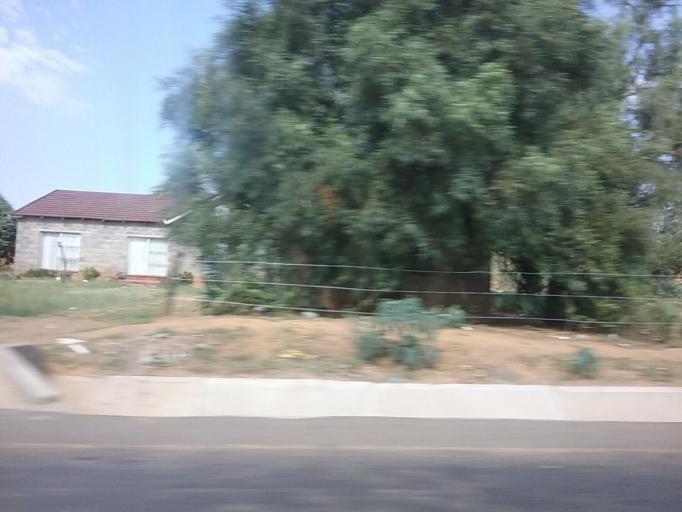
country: LS
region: Berea
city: Teyateyaneng
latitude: -29.1188
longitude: 27.9748
